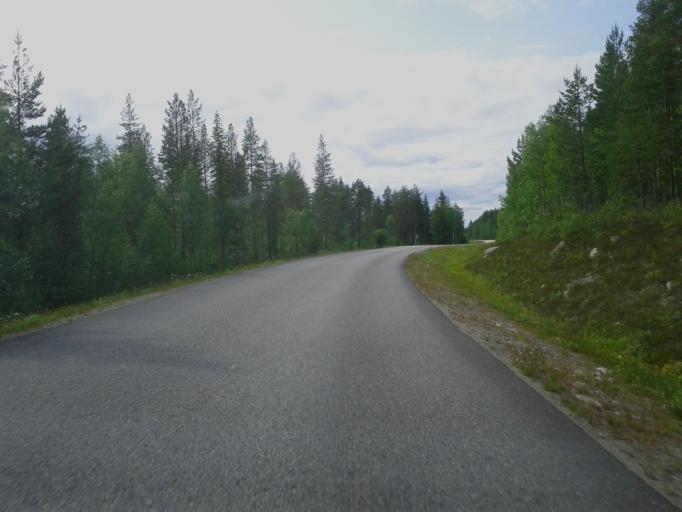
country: SE
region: Vaesterbotten
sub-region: Lycksele Kommun
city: Soderfors
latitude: 65.2756
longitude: 17.9482
